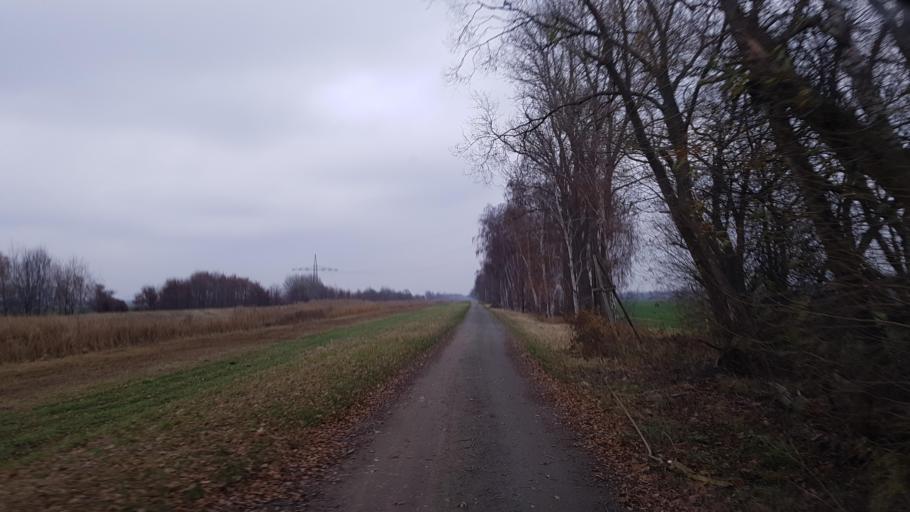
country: DE
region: Brandenburg
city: Schraden
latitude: 51.4615
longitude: 13.6691
